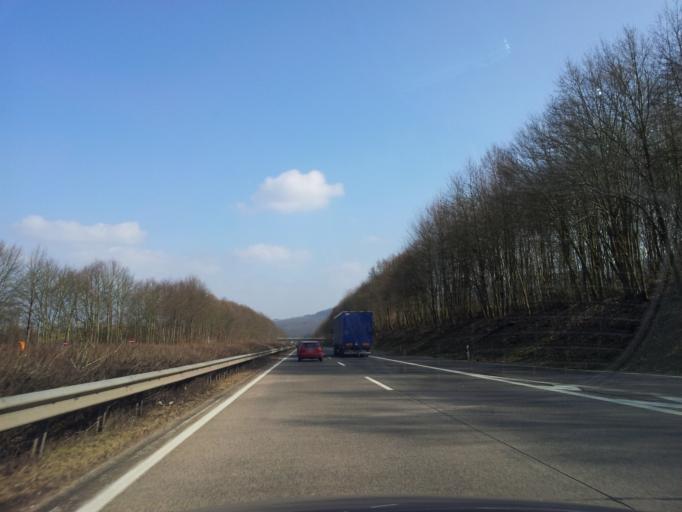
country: DE
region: Rheinland-Pfalz
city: Hetzerath
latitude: 49.8746
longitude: 6.8319
